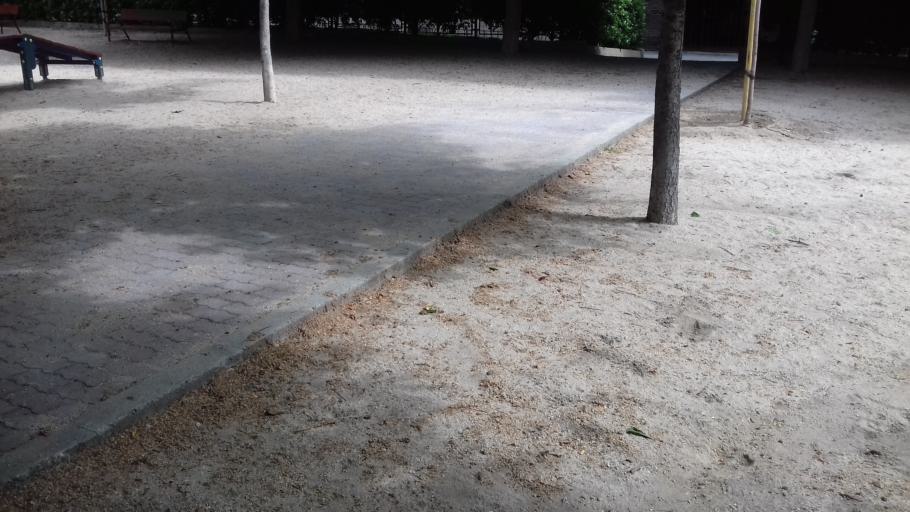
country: ES
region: Madrid
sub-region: Provincia de Madrid
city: Salamanca
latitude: 40.4187
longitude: -3.6671
